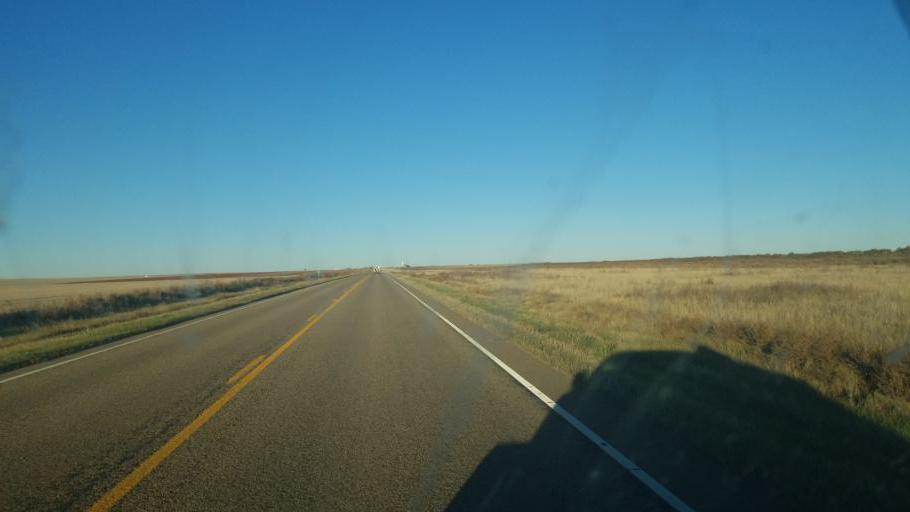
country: US
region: Colorado
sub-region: Cheyenne County
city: Cheyenne Wells
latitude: 38.8170
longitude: -102.5123
